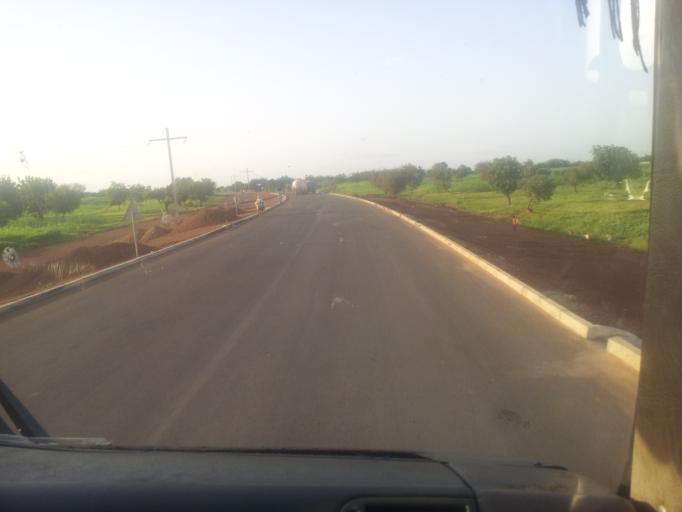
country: BF
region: Centre-Est
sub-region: Kouritenga Province
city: Koupela
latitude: 12.0141
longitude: -0.3613
